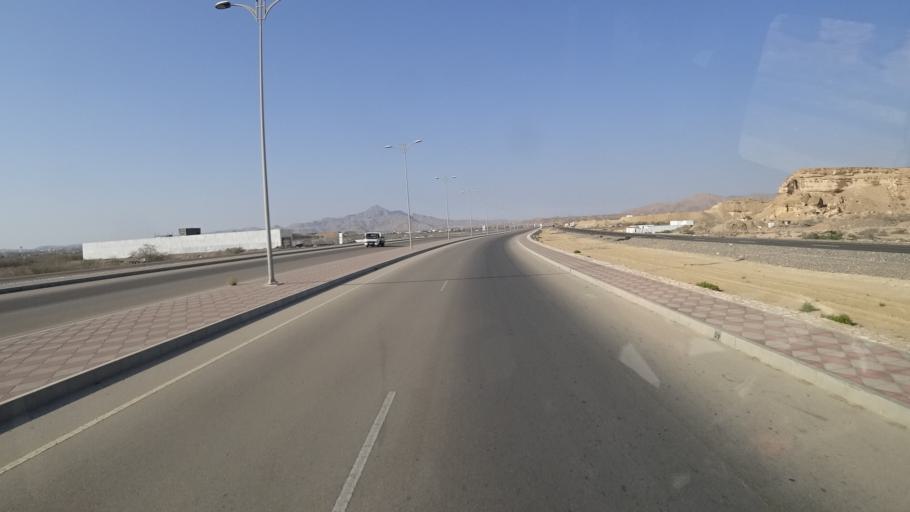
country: OM
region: Ash Sharqiyah
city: Sur
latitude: 22.5893
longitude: 59.4771
